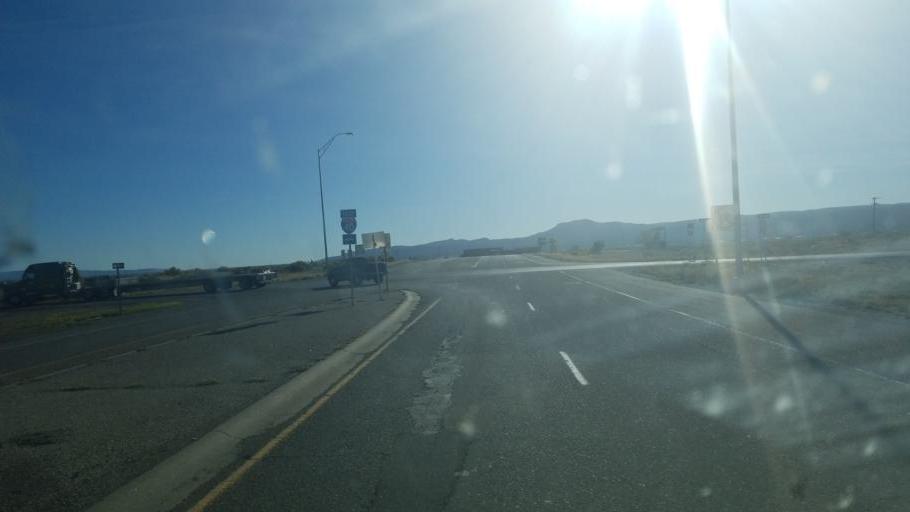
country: US
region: New Mexico
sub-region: Cibola County
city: Grants
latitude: 35.1229
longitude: -107.8308
